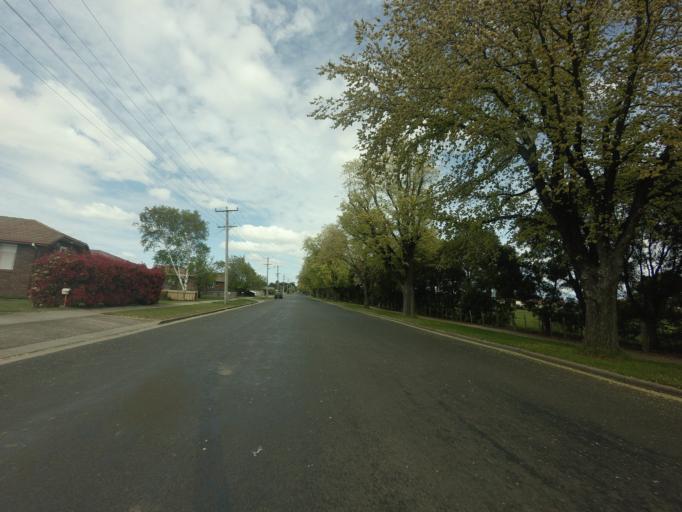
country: AU
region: Tasmania
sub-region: Northern Midlands
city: Longford
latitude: -41.6011
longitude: 147.1245
